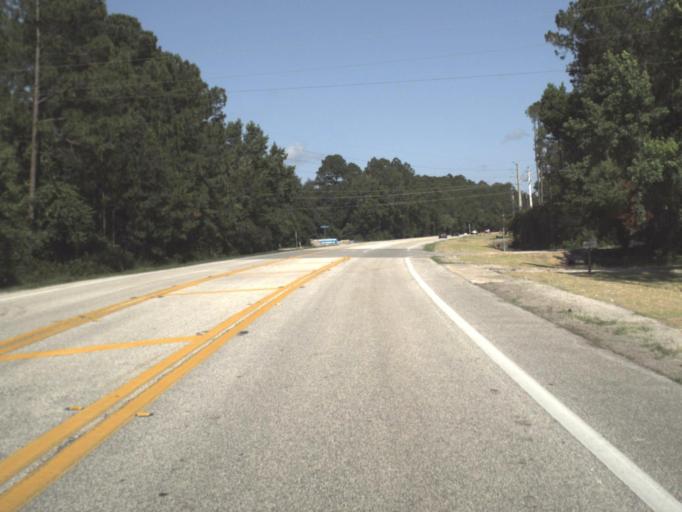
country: US
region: Florida
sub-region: Saint Johns County
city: Saint Augustine
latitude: 29.9586
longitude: -81.4649
